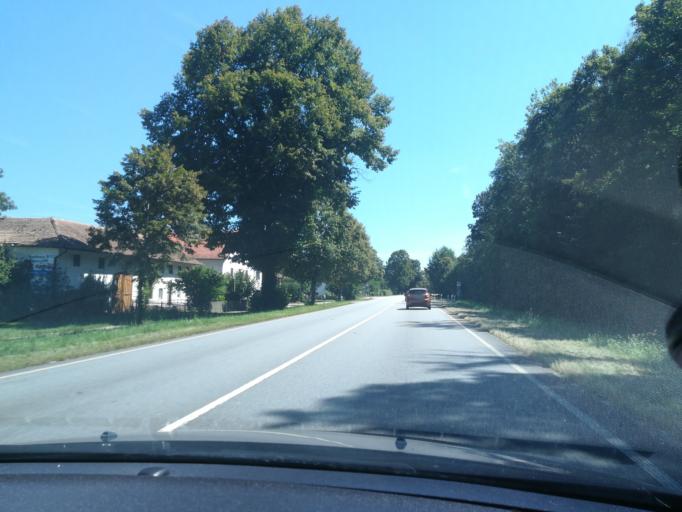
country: DE
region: Bavaria
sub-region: Upper Bavaria
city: Forstinning
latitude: 48.1626
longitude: 11.9436
